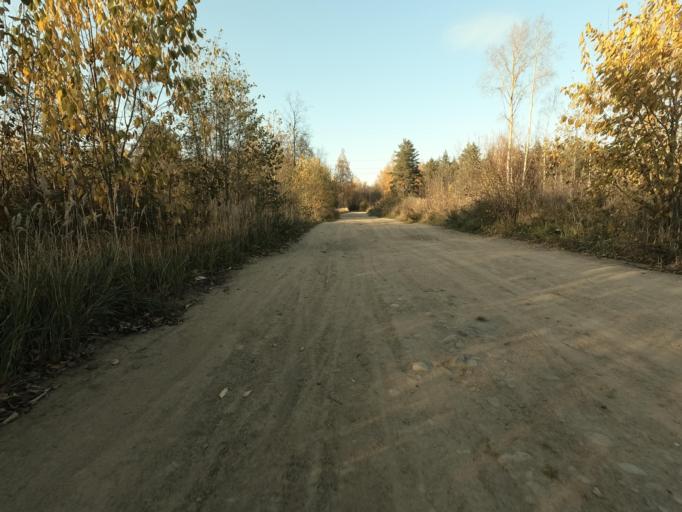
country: RU
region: Leningrad
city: Sinyavino
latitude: 59.8759
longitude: 31.0404
